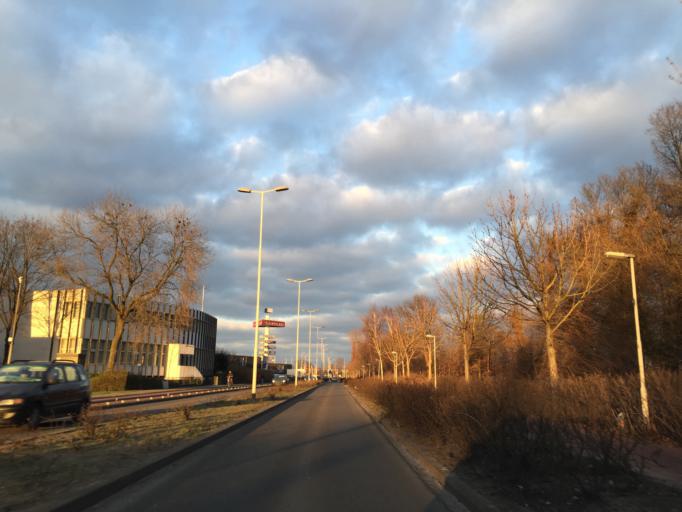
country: NL
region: South Holland
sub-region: Gemeente Rotterdam
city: Delfshaven
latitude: 51.9241
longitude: 4.4365
